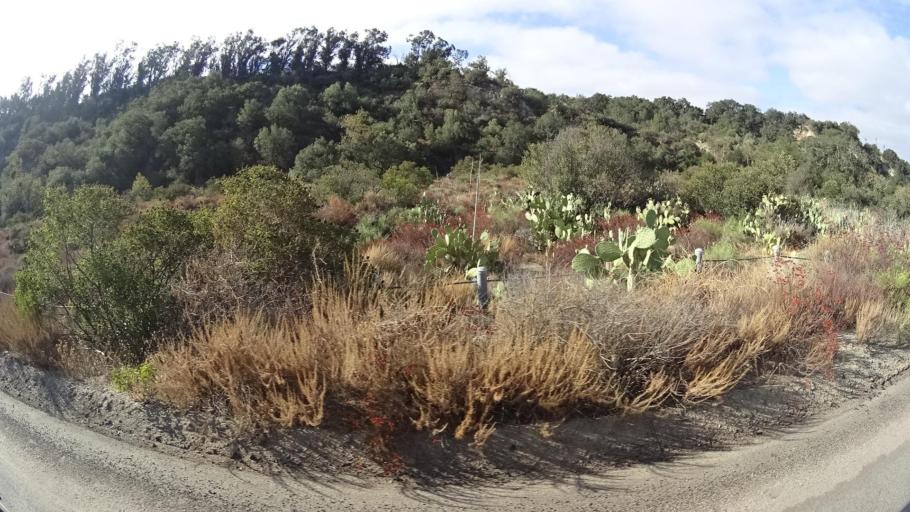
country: US
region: California
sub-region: Orange County
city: Trabuco Canyon
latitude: 33.6609
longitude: -117.5787
